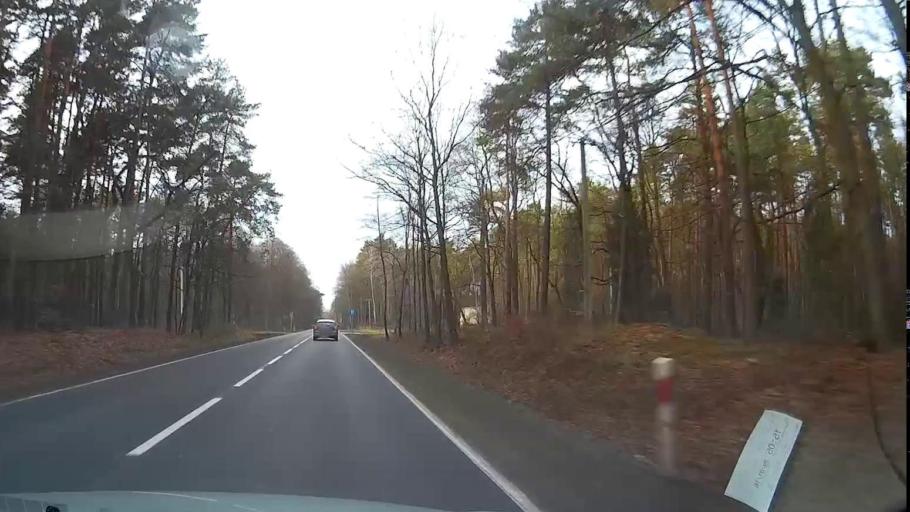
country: PL
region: Lesser Poland Voivodeship
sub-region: Powiat chrzanowski
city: Brodla
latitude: 50.0366
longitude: 19.6041
